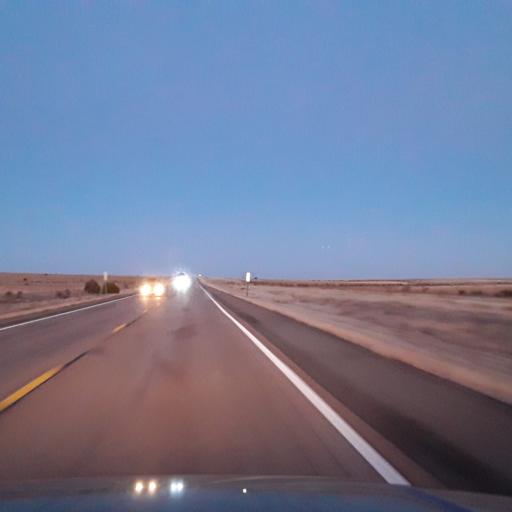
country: US
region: New Mexico
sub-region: Guadalupe County
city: Santa Rosa
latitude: 34.7649
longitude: -104.9790
